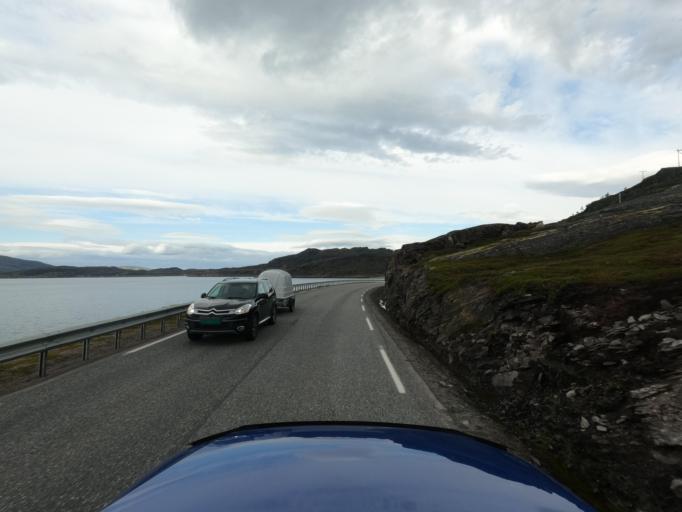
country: NO
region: Finnmark Fylke
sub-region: Hammerfest
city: Rypefjord
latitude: 70.5886
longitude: 23.6808
